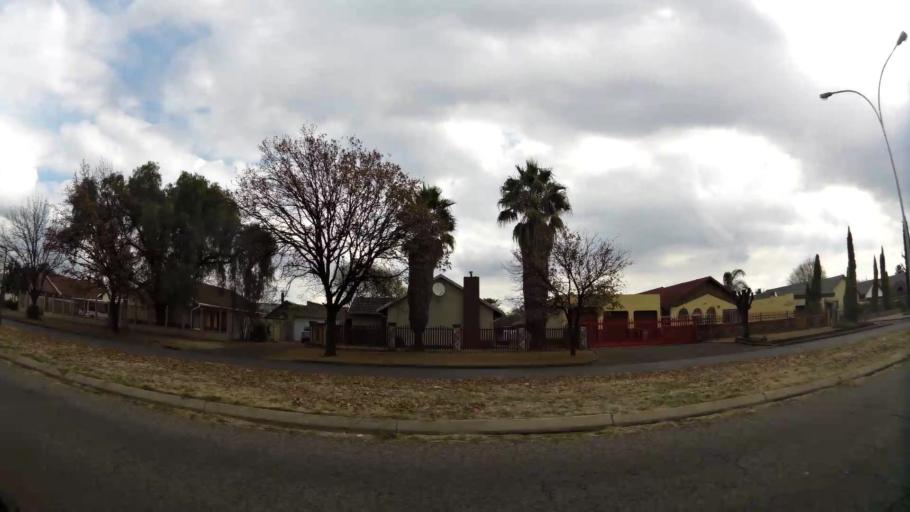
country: ZA
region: Gauteng
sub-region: Sedibeng District Municipality
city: Vanderbijlpark
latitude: -26.7279
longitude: 27.8531
